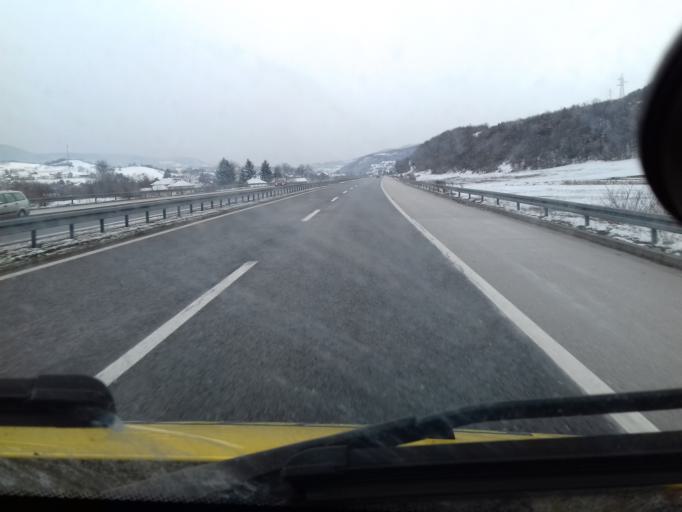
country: BA
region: Federation of Bosnia and Herzegovina
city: Mahala
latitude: 43.9880
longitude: 18.2268
